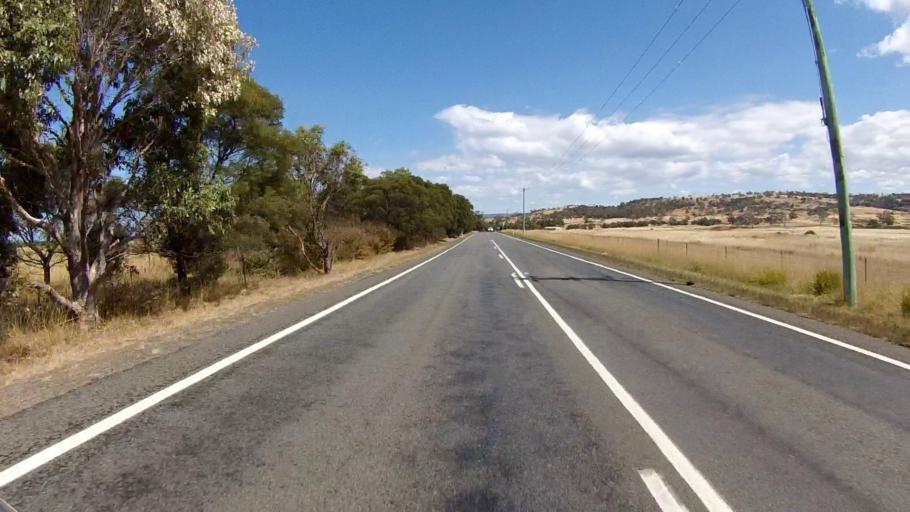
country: AU
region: Tasmania
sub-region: Break O'Day
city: St Helens
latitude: -42.1020
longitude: 148.0619
